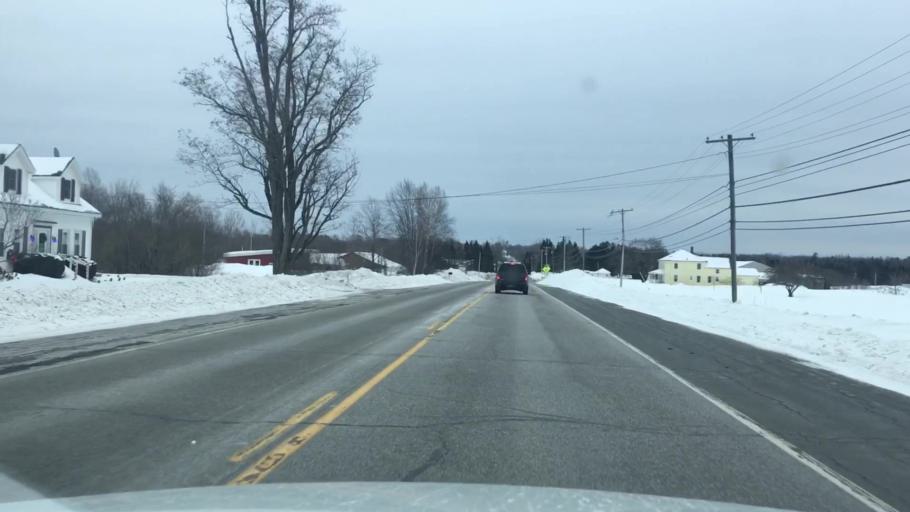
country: US
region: Maine
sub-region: Penobscot County
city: Charleston
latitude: 45.0198
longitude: -69.0287
